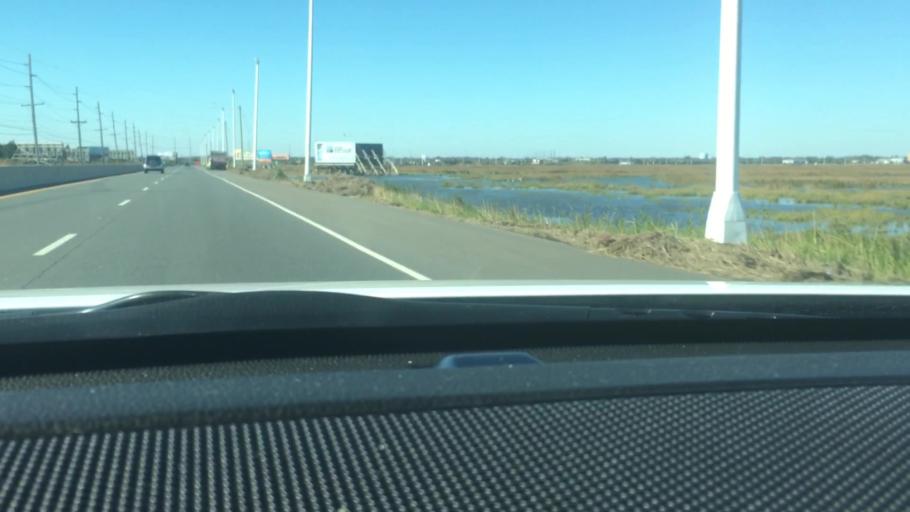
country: US
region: New Jersey
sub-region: Atlantic County
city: Absecon
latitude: 39.3890
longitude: -74.4802
